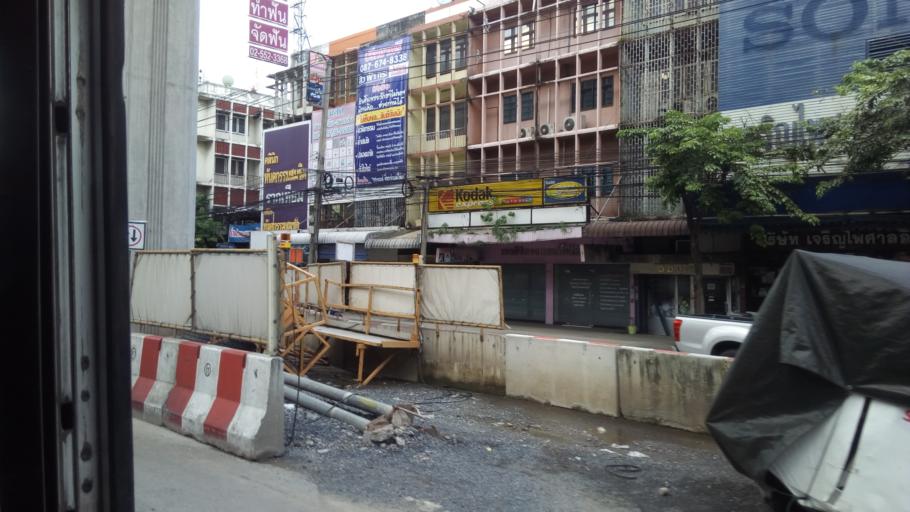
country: TH
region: Bangkok
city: Bang Khen
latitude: 13.8932
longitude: 100.6073
